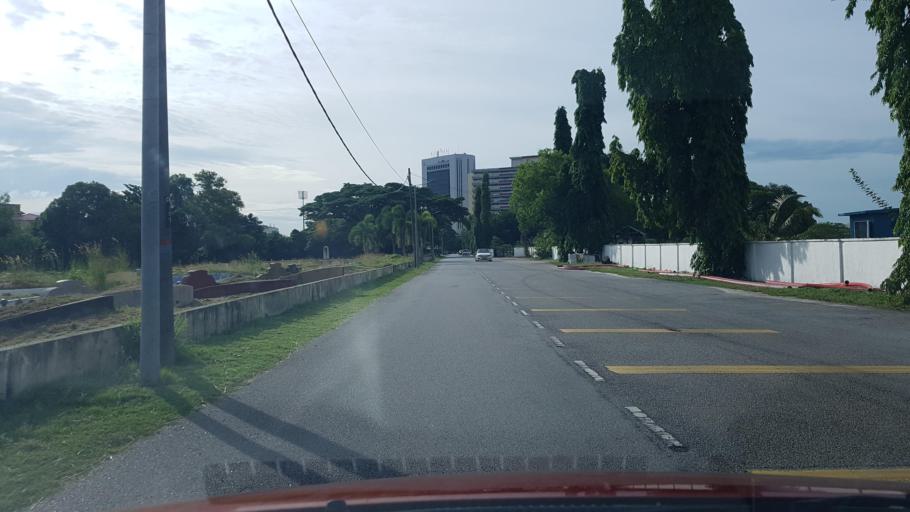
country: MY
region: Terengganu
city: Kuala Terengganu
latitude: 5.3252
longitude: 103.1440
